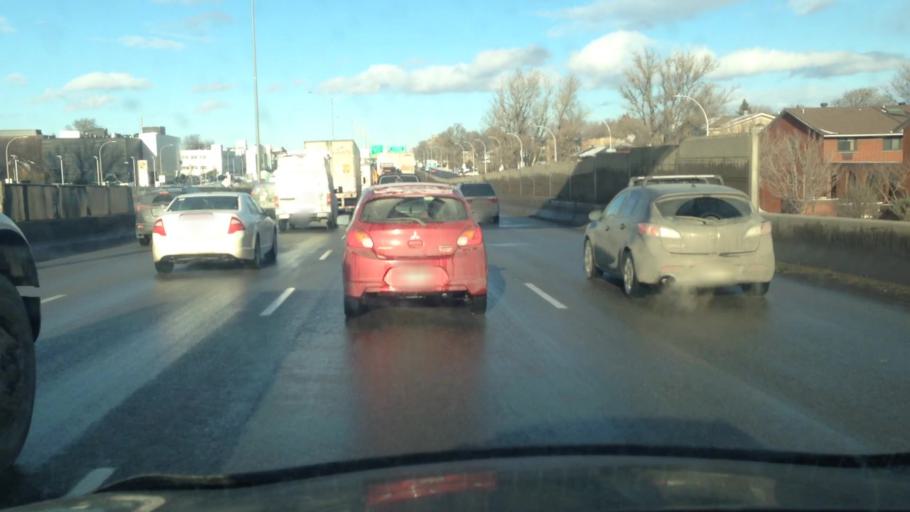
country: CA
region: Quebec
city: Saint-Laurent
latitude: 45.5095
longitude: -73.6618
